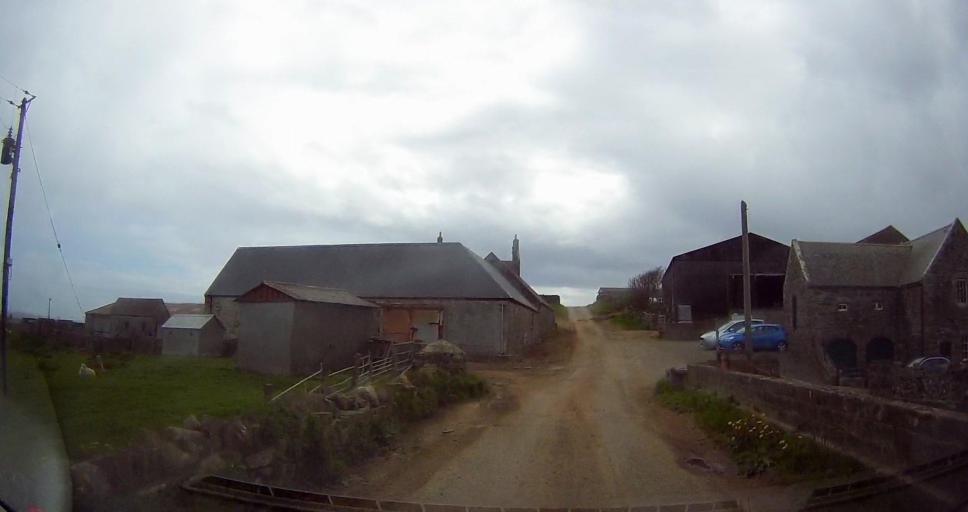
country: GB
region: Scotland
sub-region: Shetland Islands
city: Sandwick
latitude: 59.9025
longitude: -1.3377
